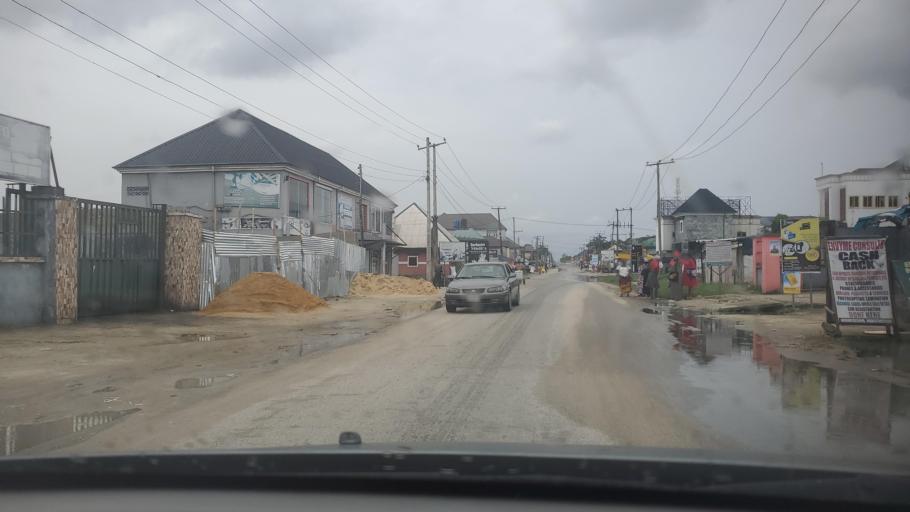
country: NG
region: Rivers
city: Port Harcourt
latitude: 4.8673
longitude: 6.9815
